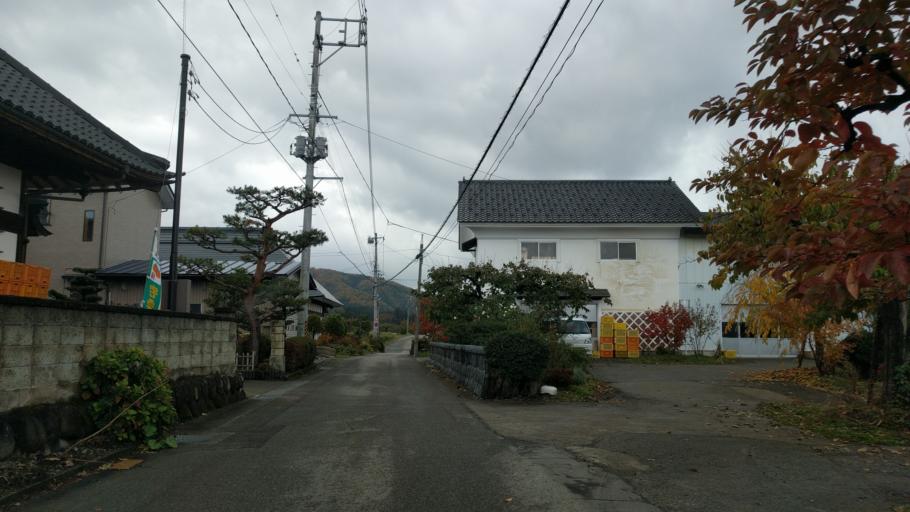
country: JP
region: Fukushima
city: Kitakata
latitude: 37.4610
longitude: 139.9318
